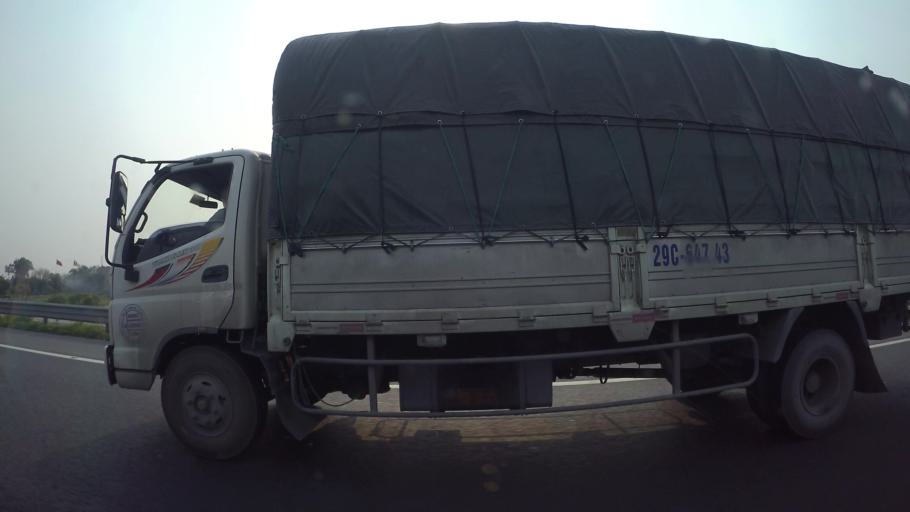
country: VN
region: Ha Noi
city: Van Dien
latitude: 20.9180
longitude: 105.8596
